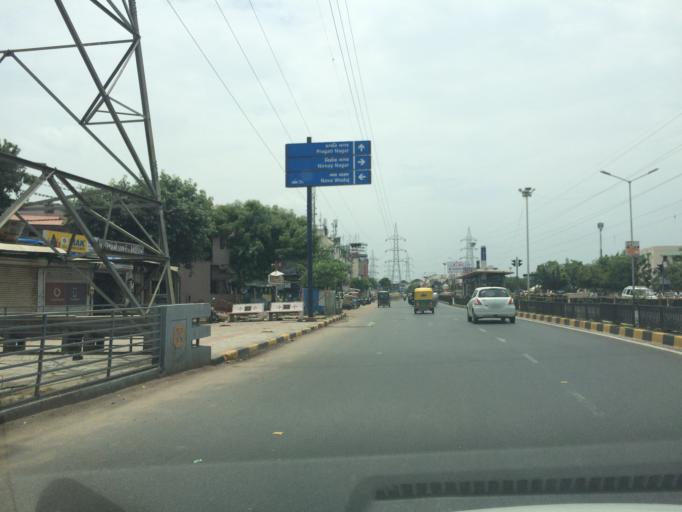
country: IN
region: Gujarat
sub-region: Ahmadabad
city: Ahmedabad
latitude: 23.0676
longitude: 72.5649
